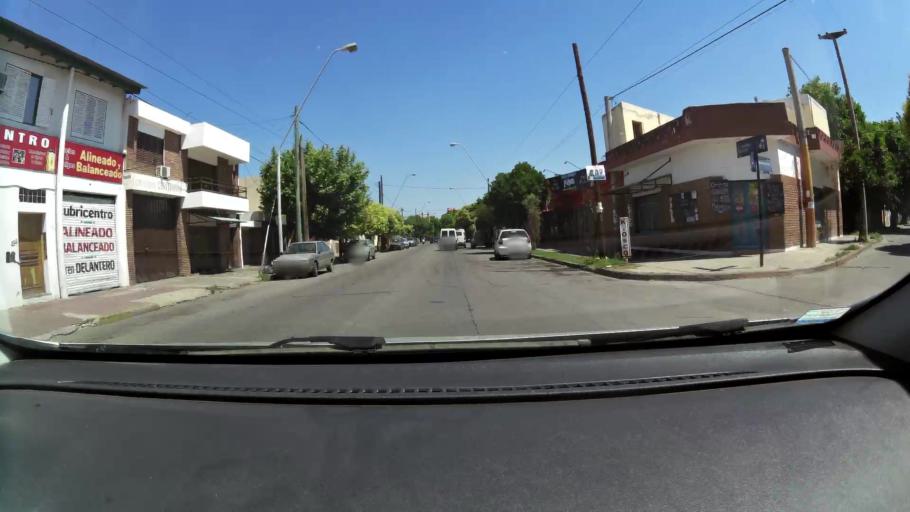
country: AR
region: Cordoba
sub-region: Departamento de Capital
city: Cordoba
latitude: -31.3864
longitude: -64.1962
